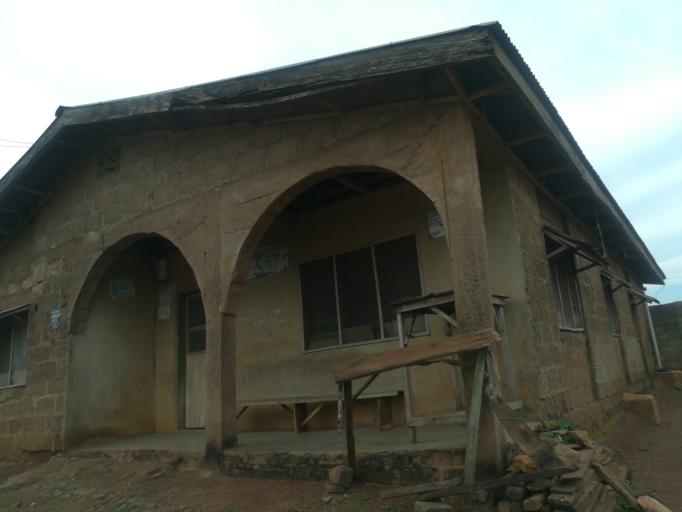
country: NG
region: Oyo
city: Ibadan
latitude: 7.3743
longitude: 3.9531
